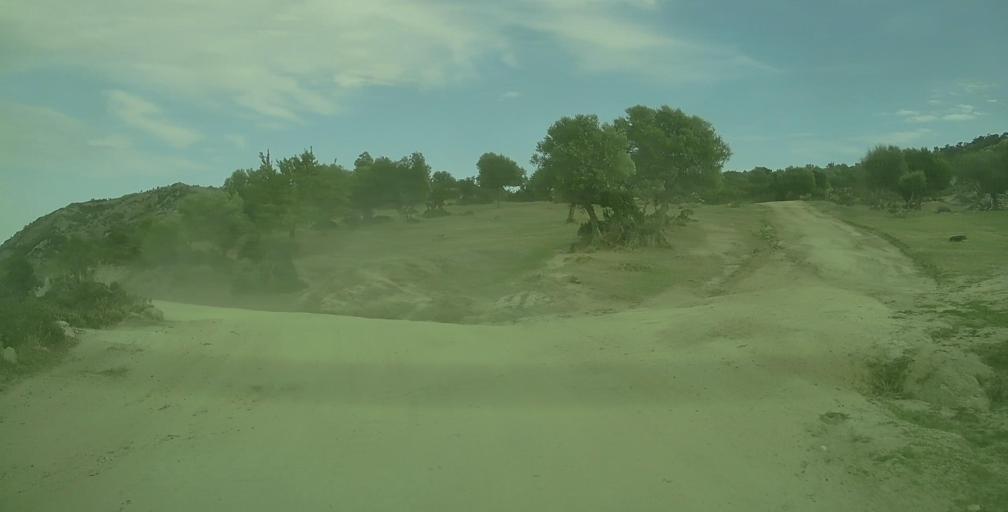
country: GR
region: Central Macedonia
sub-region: Nomos Chalkidikis
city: Sykia
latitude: 40.0138
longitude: 23.9341
